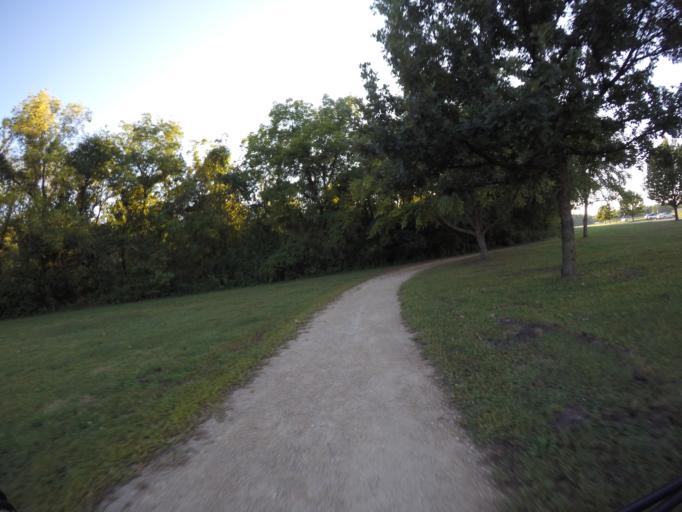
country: US
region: Kansas
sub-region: Riley County
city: Manhattan
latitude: 39.1823
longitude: -96.6295
